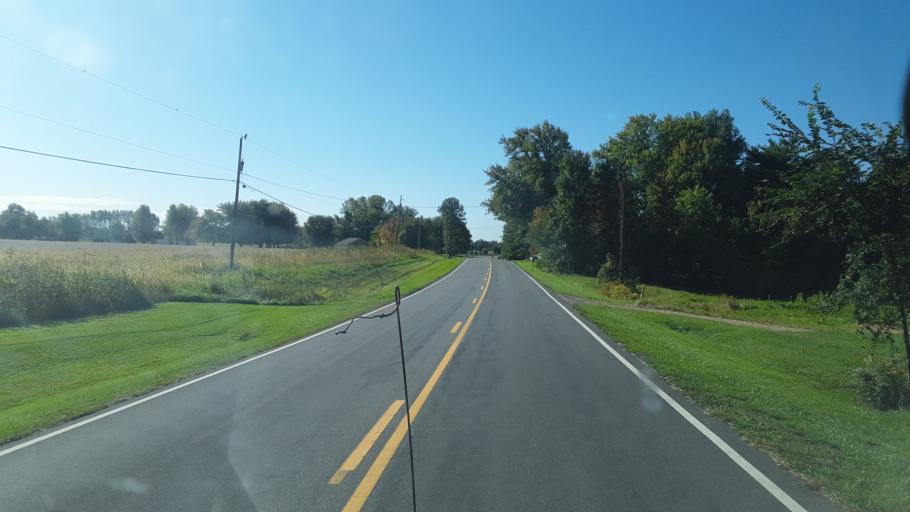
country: US
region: Ohio
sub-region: Delaware County
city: Sunbury
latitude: 40.2348
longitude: -82.7898
